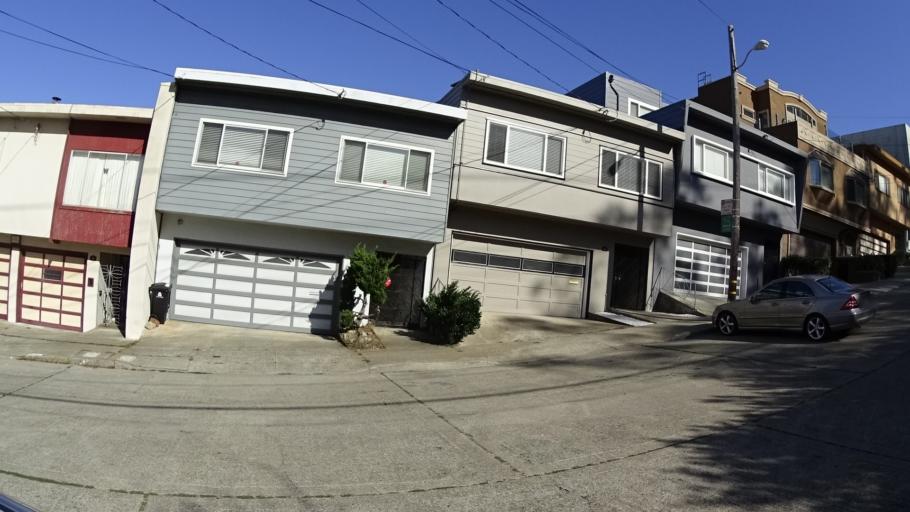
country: US
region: California
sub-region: San Mateo County
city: Brisbane
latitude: 37.7209
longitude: -122.4118
